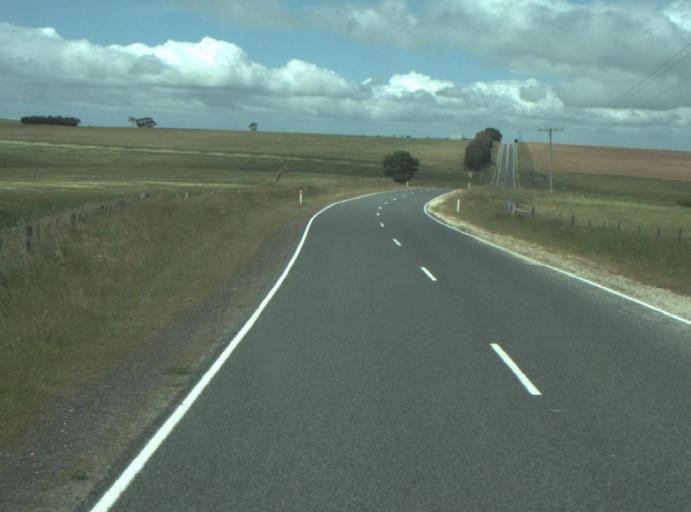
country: AU
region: Victoria
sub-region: Greater Geelong
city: Wandana Heights
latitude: -38.1771
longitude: 144.2710
